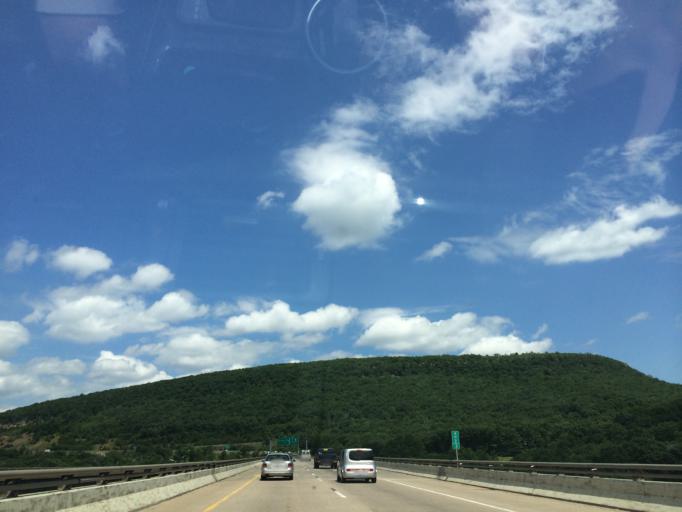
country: US
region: Pennsylvania
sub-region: Lackawanna County
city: Dunmore
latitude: 41.3943
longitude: -75.5833
